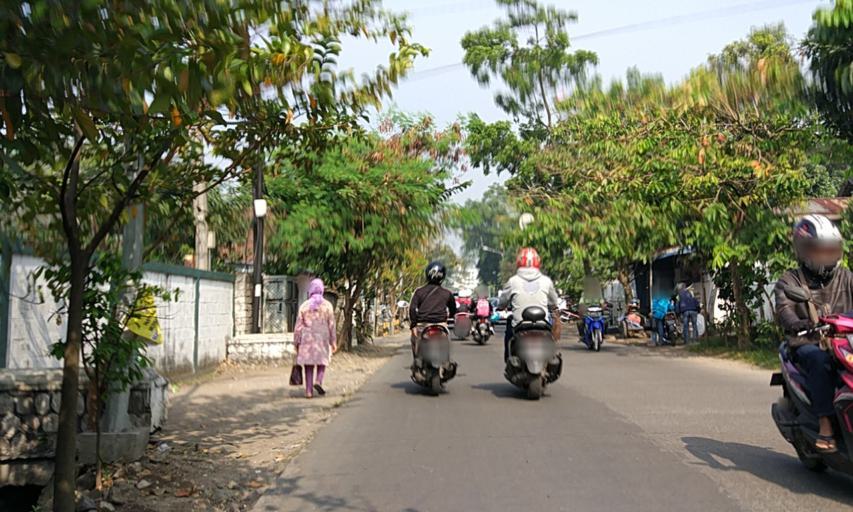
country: ID
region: West Java
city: Bandung
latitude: -6.9017
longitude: 107.6356
